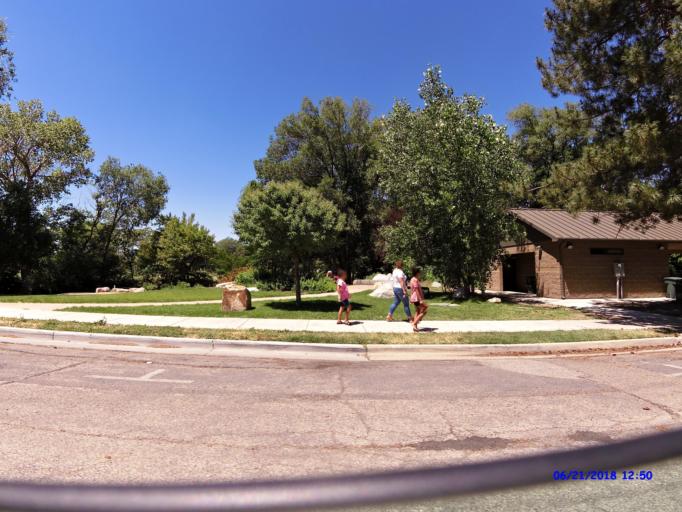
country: US
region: Utah
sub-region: Weber County
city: Ogden
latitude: 41.2336
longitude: -111.9731
